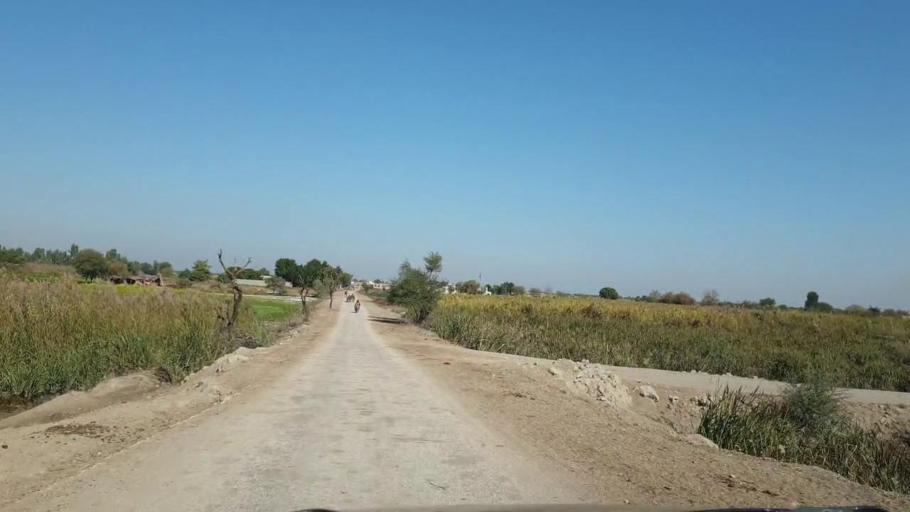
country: PK
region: Sindh
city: Sinjhoro
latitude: 26.1061
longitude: 68.8427
